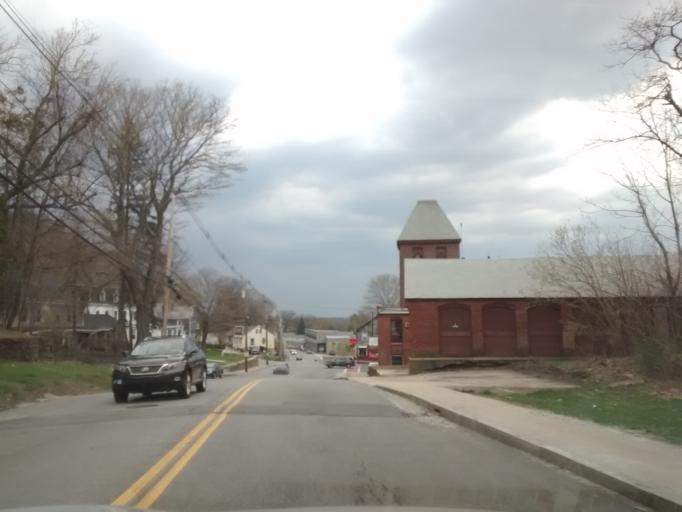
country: US
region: Massachusetts
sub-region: Worcester County
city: Millbury
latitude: 42.1788
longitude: -71.7721
